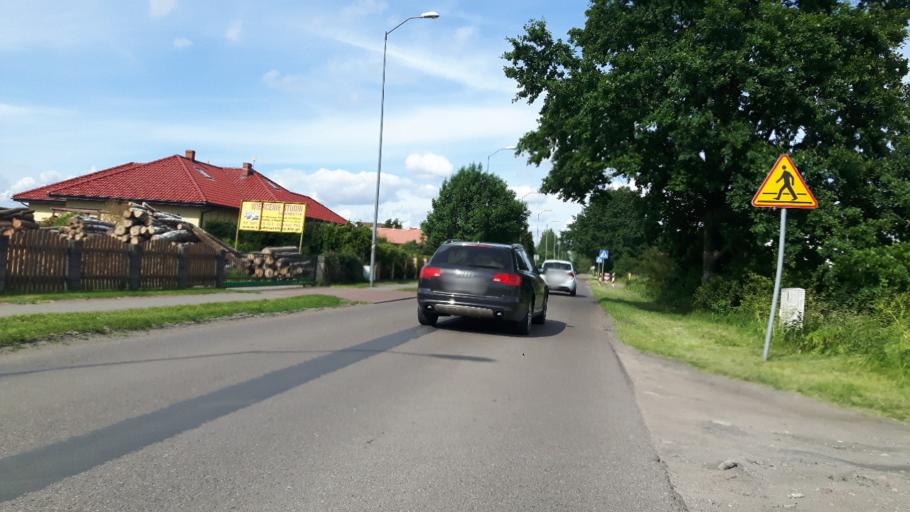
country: PL
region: West Pomeranian Voivodeship
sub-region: Powiat goleniowski
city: Goleniow
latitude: 53.4375
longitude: 14.7349
